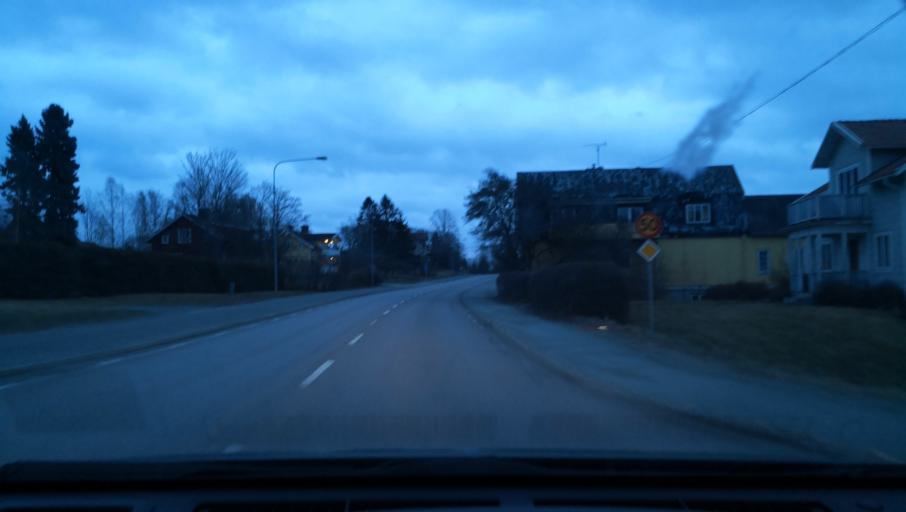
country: SE
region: Vaestmanland
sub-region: Kopings Kommun
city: Kolsva
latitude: 59.5926
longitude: 15.8536
